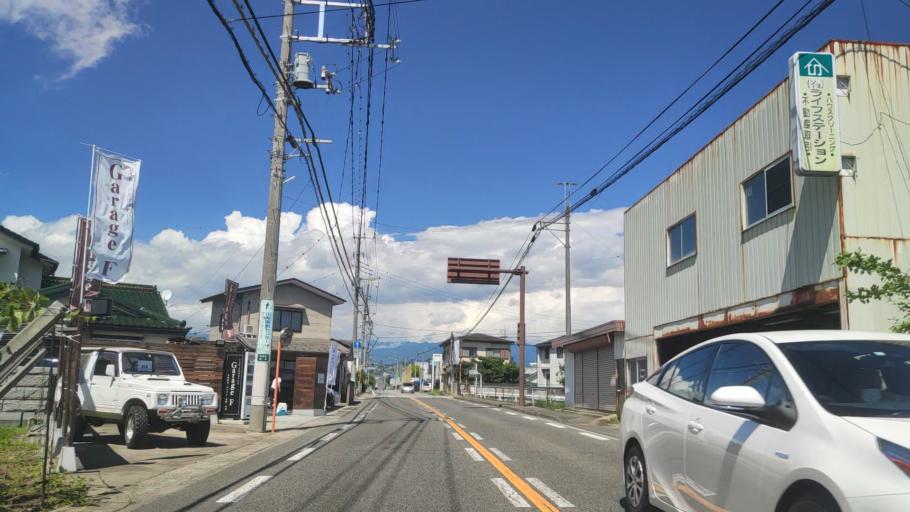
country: JP
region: Yamanashi
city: Isawa
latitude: 35.6624
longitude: 138.6413
